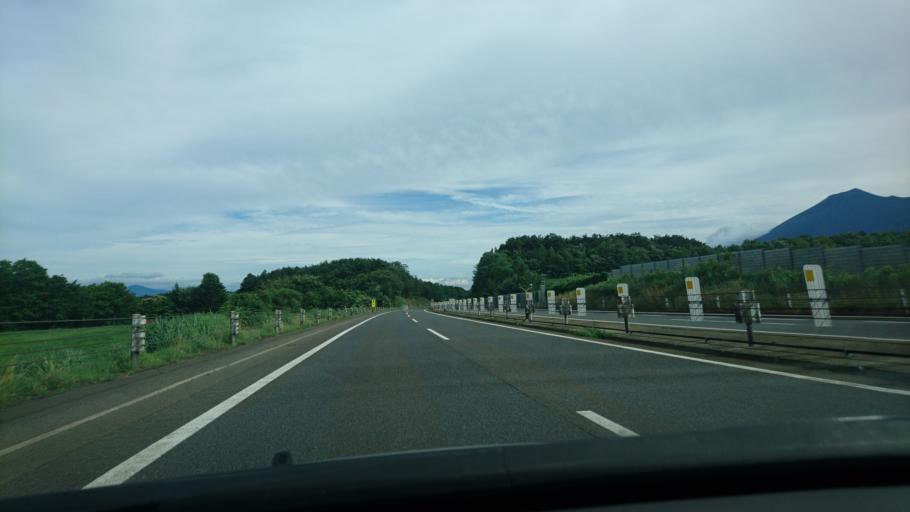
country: JP
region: Iwate
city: Shizukuishi
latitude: 39.9674
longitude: 141.0286
